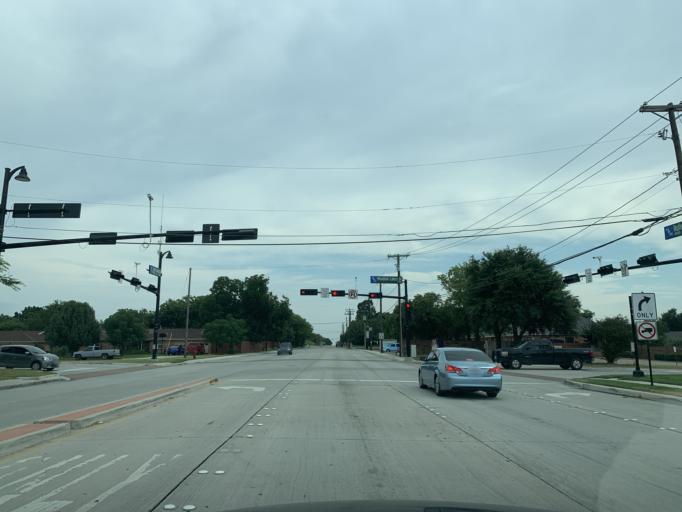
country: US
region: Texas
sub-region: Tarrant County
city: North Richland Hills
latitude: 32.8385
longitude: -97.2388
